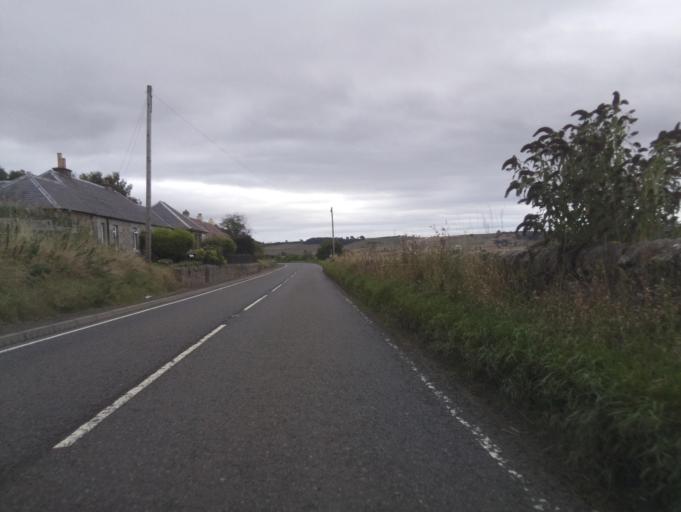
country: GB
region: Scotland
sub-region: Fife
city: Ballingry
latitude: 56.1996
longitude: -3.3028
